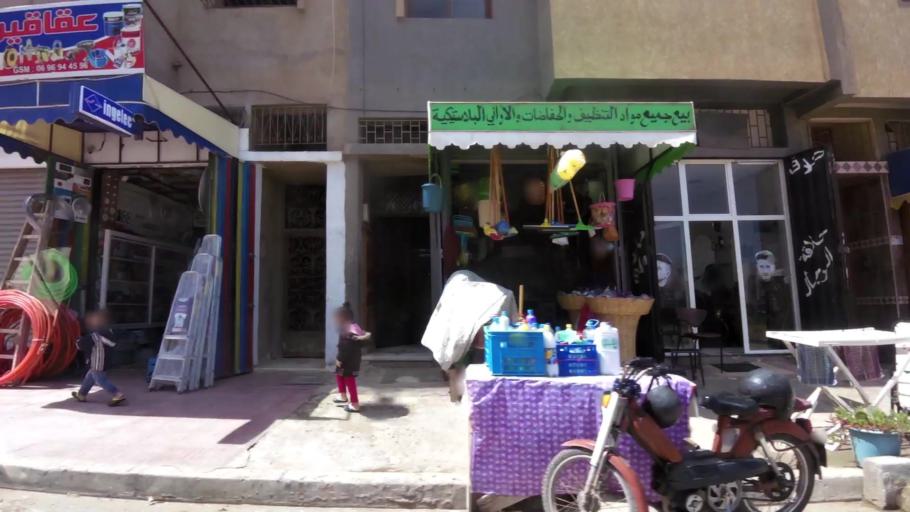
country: MA
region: Grand Casablanca
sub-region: Nouaceur
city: Dar Bouazza
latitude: 33.5314
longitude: -7.7332
